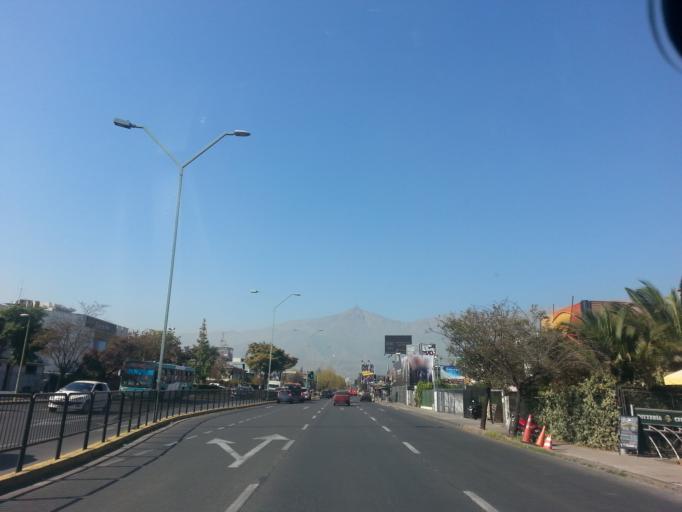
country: CL
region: Santiago Metropolitan
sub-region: Provincia de Santiago
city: Villa Presidente Frei, Nunoa, Santiago, Chile
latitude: -33.4315
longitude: -70.5799
